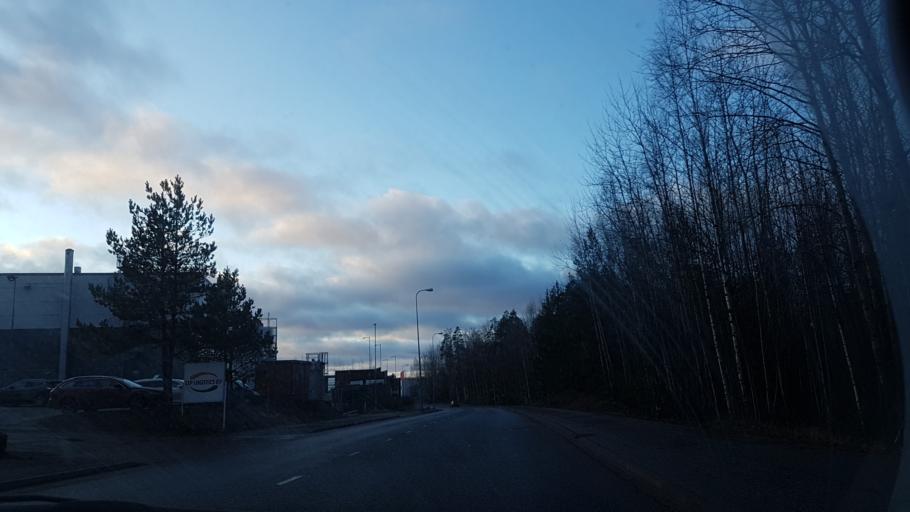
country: FI
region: Uusimaa
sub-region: Helsinki
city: Kilo
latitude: 60.3100
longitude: 24.8531
